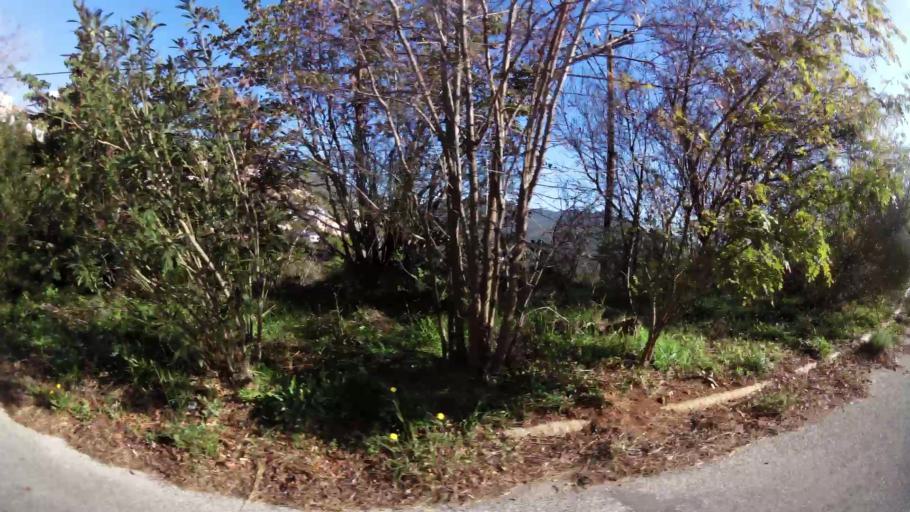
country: GR
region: Attica
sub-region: Nomarchia Anatolikis Attikis
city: Dhrafi
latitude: 38.0327
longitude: 23.8942
